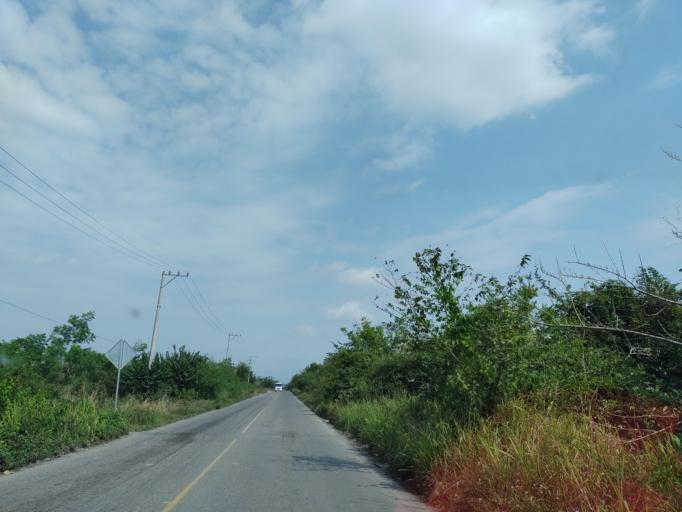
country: MX
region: Puebla
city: Espinal
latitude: 20.2791
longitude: -97.3308
